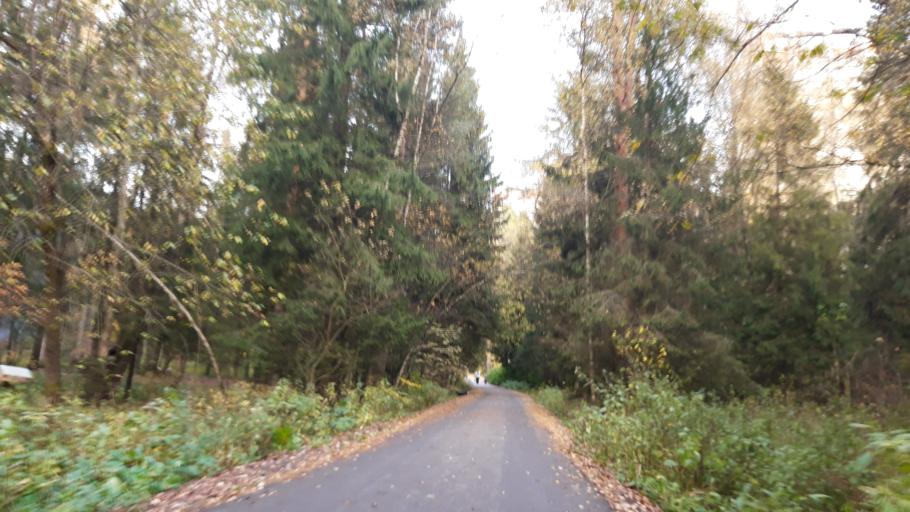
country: RU
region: Moscow
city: Zelenograd
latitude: 56.0000
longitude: 37.1839
